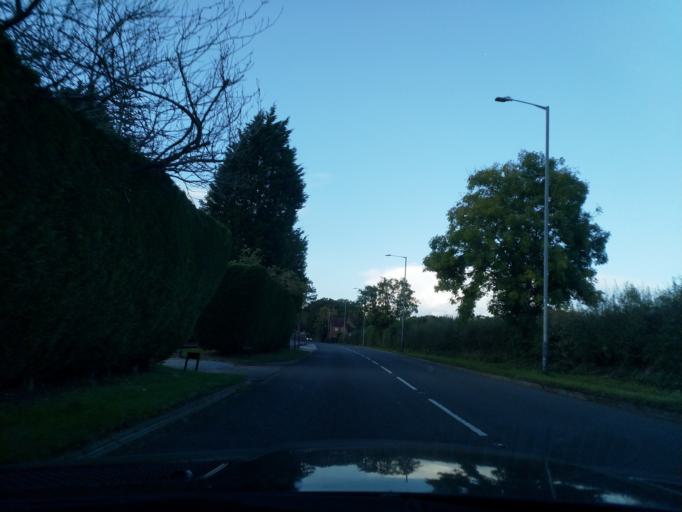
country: GB
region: England
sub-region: Solihull
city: Cheswick Green
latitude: 52.3454
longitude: -1.7759
